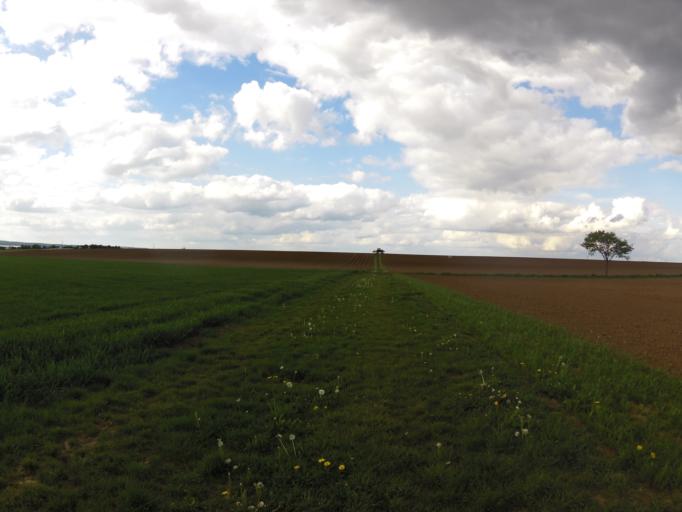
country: DE
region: Bavaria
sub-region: Regierungsbezirk Unterfranken
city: Oberpleichfeld
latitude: 49.8632
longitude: 10.0751
